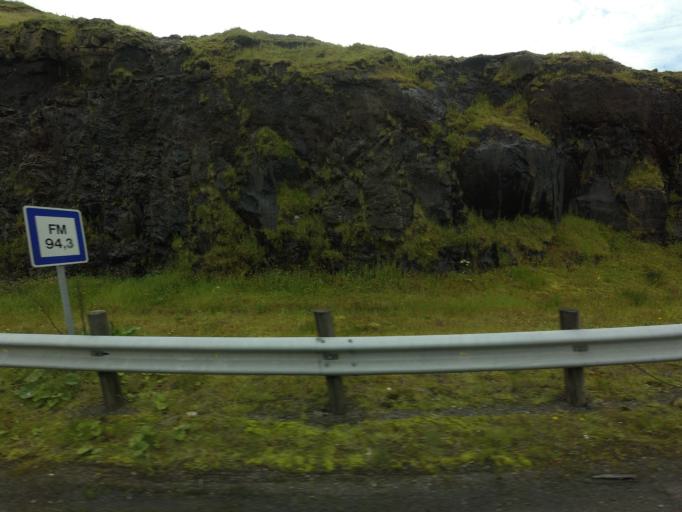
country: FO
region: Nordoyar
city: Klaksvik
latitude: 62.2183
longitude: -6.5741
